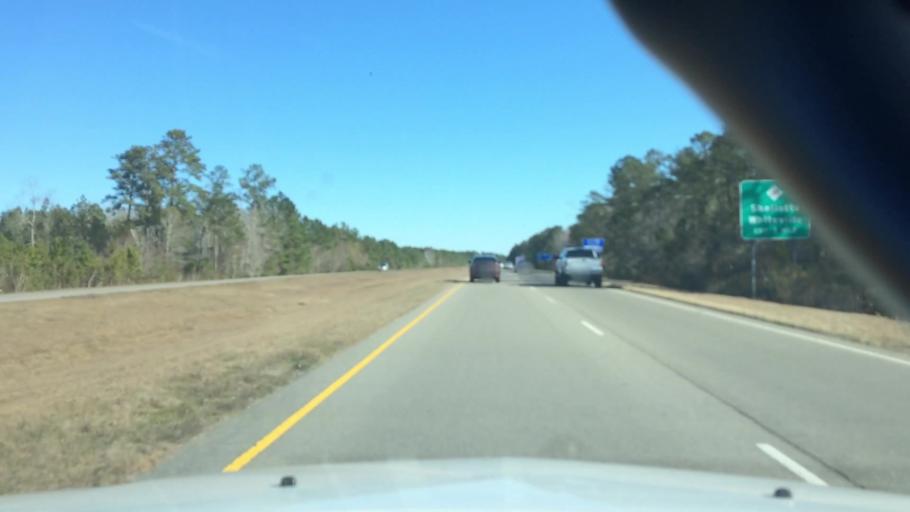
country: US
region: North Carolina
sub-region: Brunswick County
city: Shallotte
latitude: 33.9642
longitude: -78.4153
